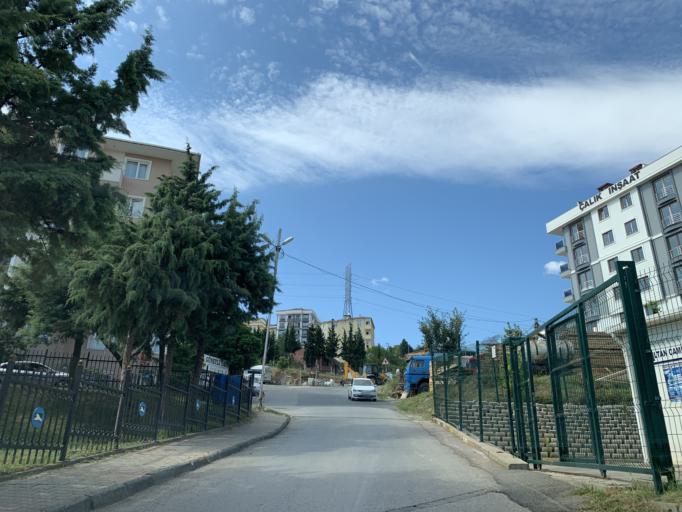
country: TR
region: Istanbul
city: Pendik
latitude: 40.8942
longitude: 29.2433
